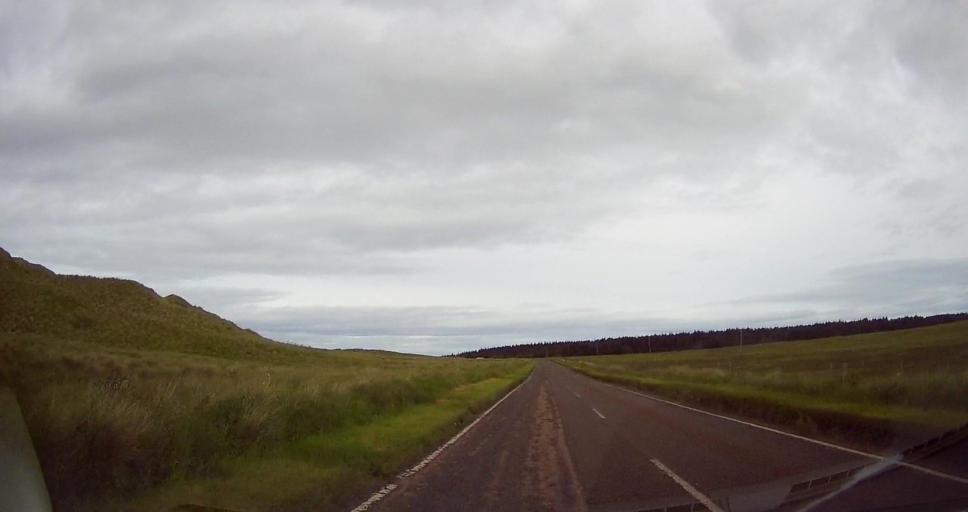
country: GB
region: Scotland
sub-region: Highland
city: Thurso
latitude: 58.6049
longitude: -3.3466
